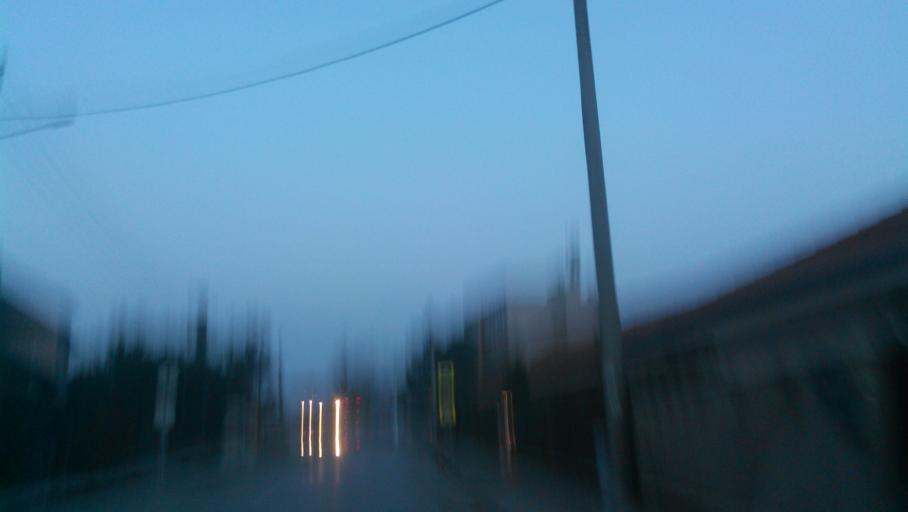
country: SK
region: Bratislavsky
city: Modra
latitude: 48.3020
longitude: 17.3407
